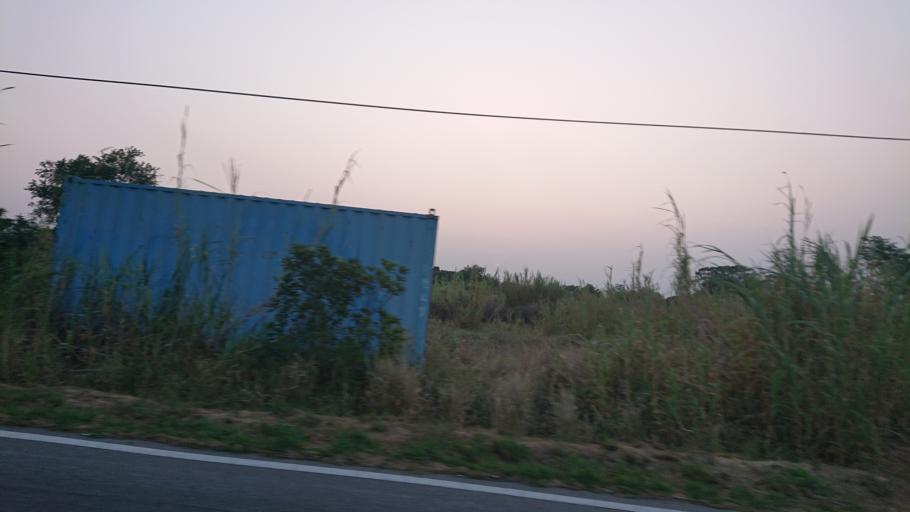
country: TW
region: Fukien
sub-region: Kinmen
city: Jincheng
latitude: 24.4528
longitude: 118.3162
